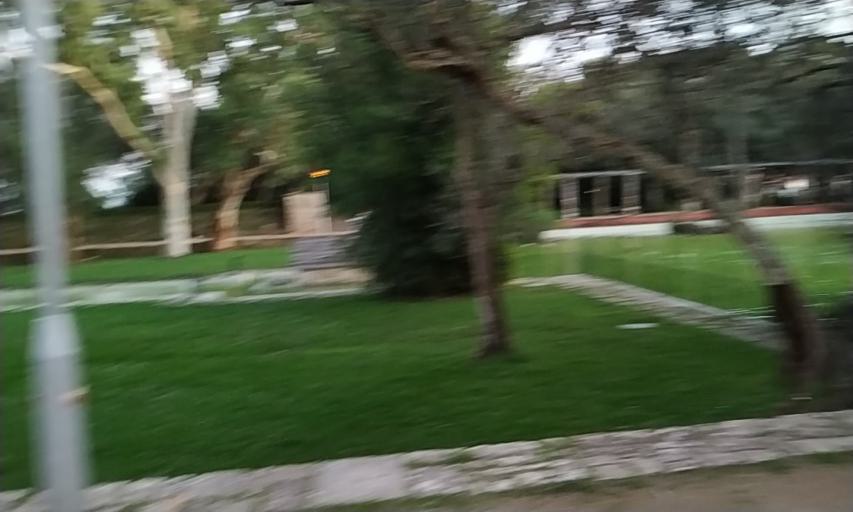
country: PT
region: Lisbon
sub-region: Oeiras
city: Alges
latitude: 38.7170
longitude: -9.2025
